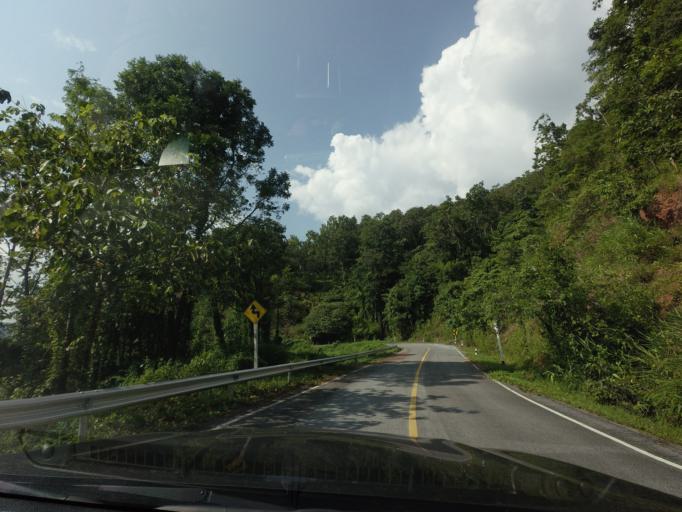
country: TH
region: Uttaradit
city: Ban Khok
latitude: 18.2493
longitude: 100.9980
